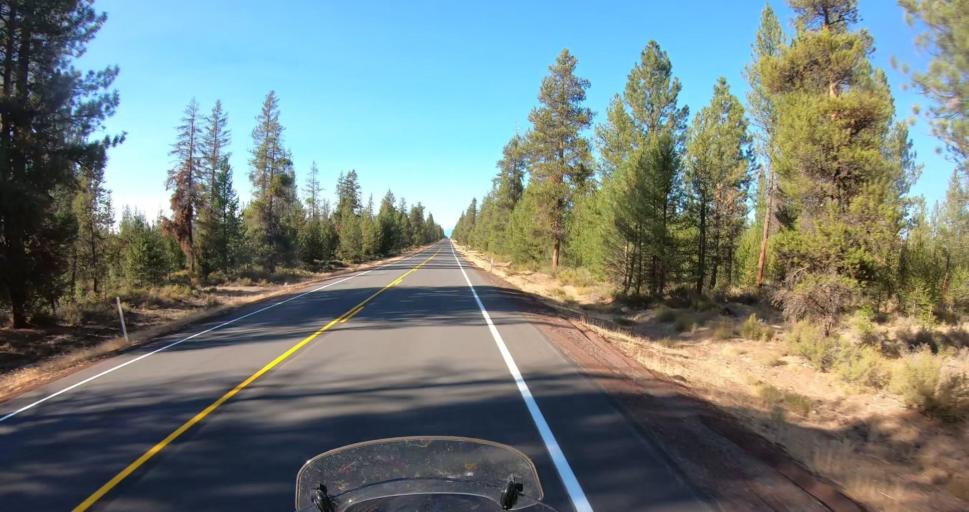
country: US
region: Oregon
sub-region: Deschutes County
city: La Pine
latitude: 43.5131
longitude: -121.4518
